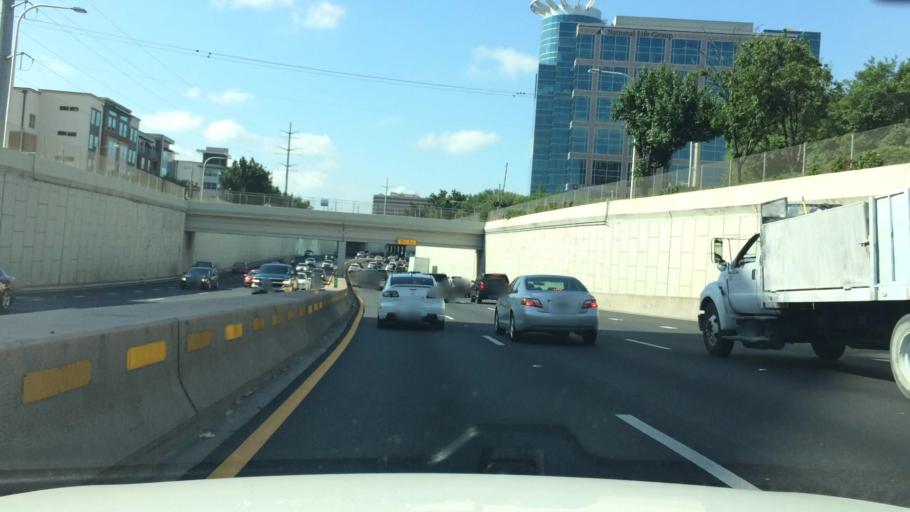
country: US
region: Texas
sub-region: Dallas County
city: Addison
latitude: 32.9623
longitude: -96.8216
